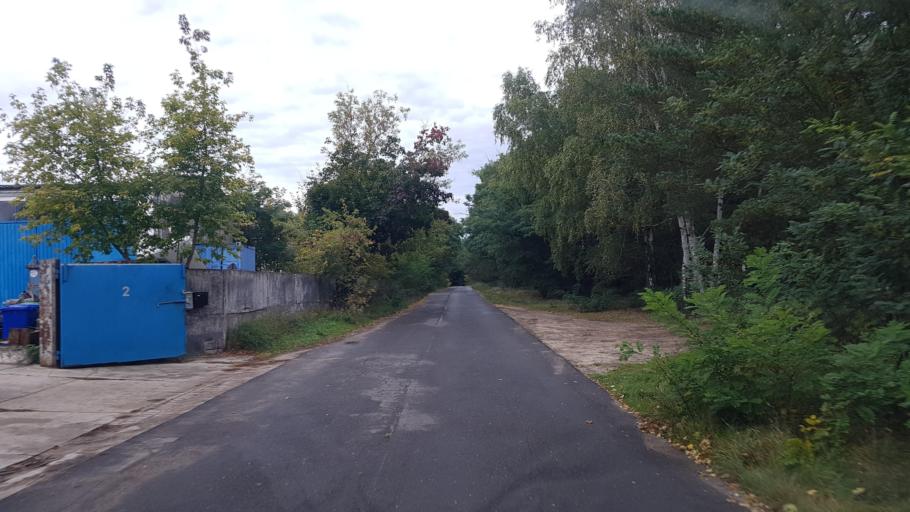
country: DE
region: Brandenburg
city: Zossen
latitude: 52.1591
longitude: 13.4855
